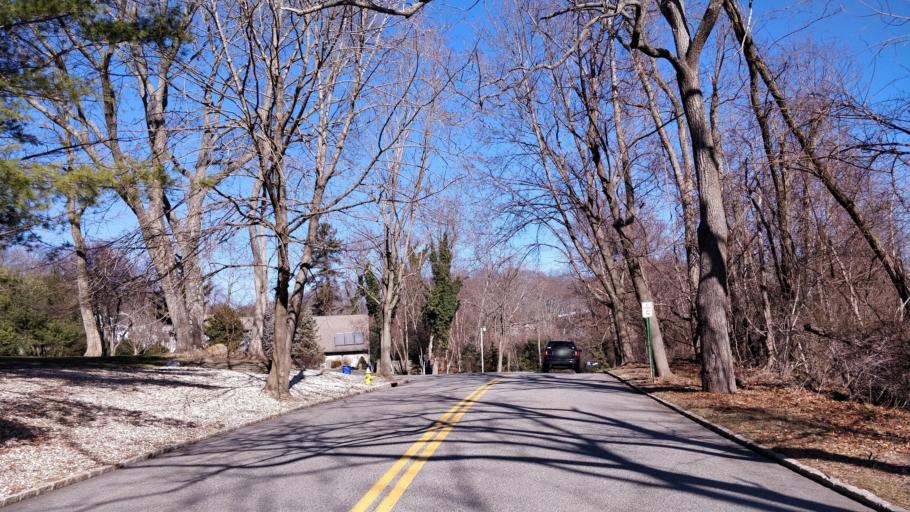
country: US
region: New York
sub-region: Suffolk County
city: Mount Sinai
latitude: 40.9562
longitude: -73.0458
